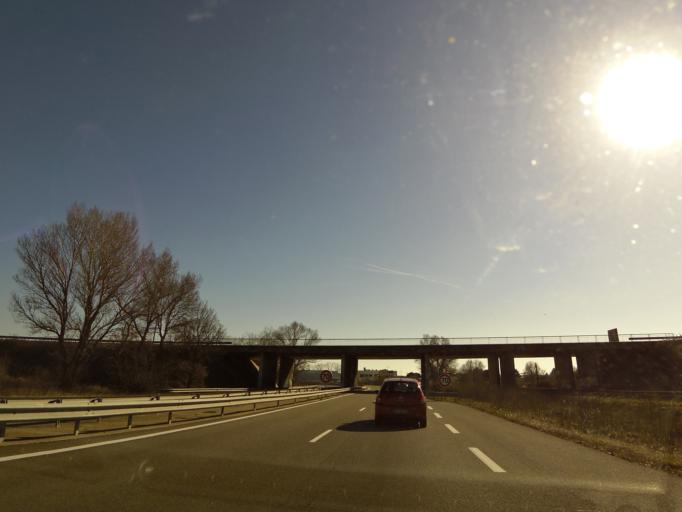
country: FR
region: Languedoc-Roussillon
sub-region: Departement du Gard
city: Aigues-Mortes
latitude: 43.5807
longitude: 4.1977
